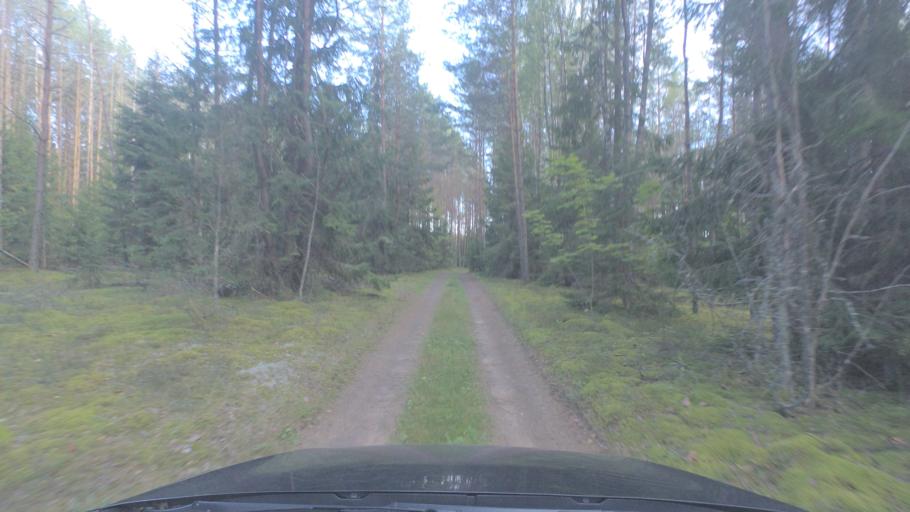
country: LT
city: Svencioneliai
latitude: 55.1607
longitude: 25.8521
